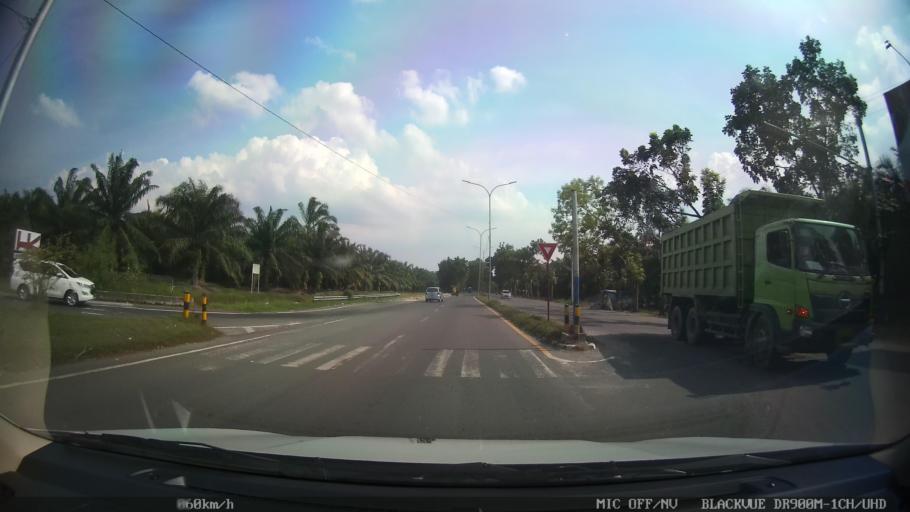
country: ID
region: North Sumatra
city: Binjai
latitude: 3.6456
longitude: 98.5355
